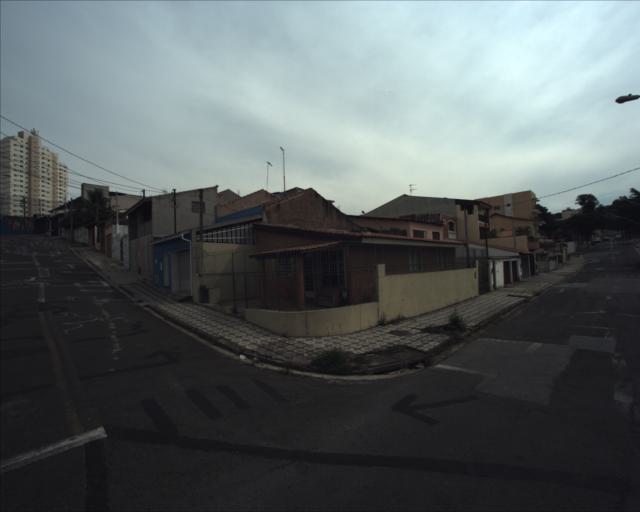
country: BR
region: Sao Paulo
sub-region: Sorocaba
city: Sorocaba
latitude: -23.4909
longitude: -47.4668
